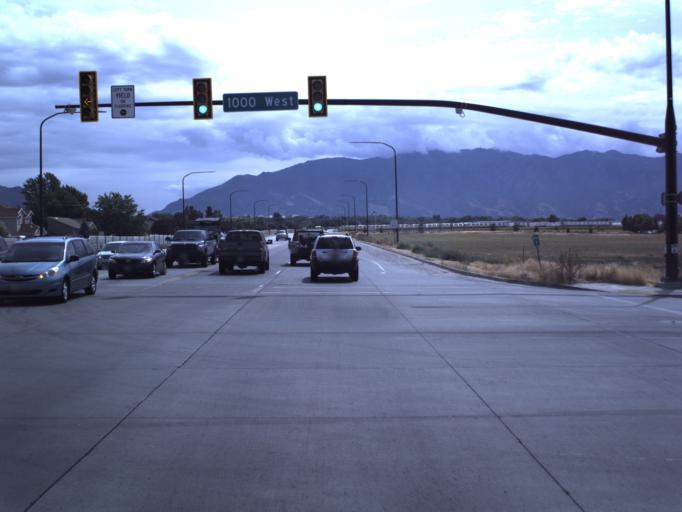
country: US
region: Utah
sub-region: Davis County
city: Clearfield
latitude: 41.1106
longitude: -112.0454
